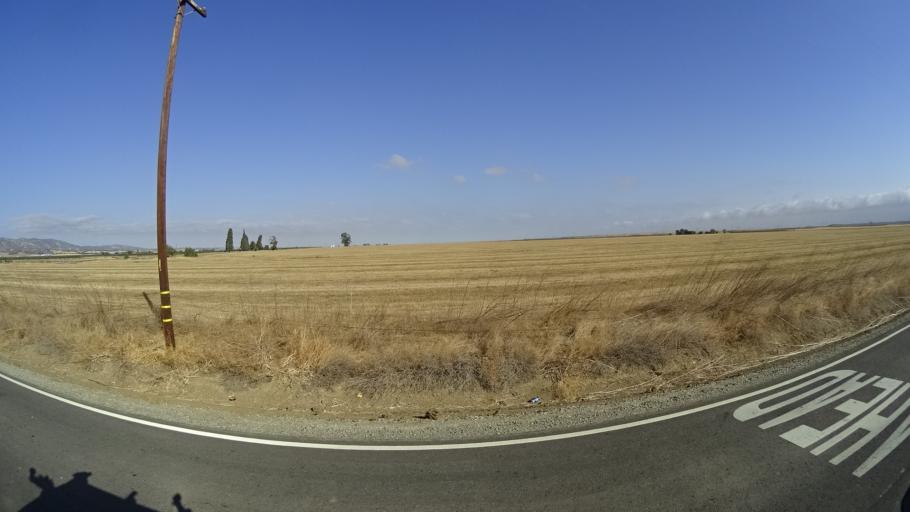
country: US
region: California
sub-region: Yolo County
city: Esparto
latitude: 38.7811
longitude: -122.0416
